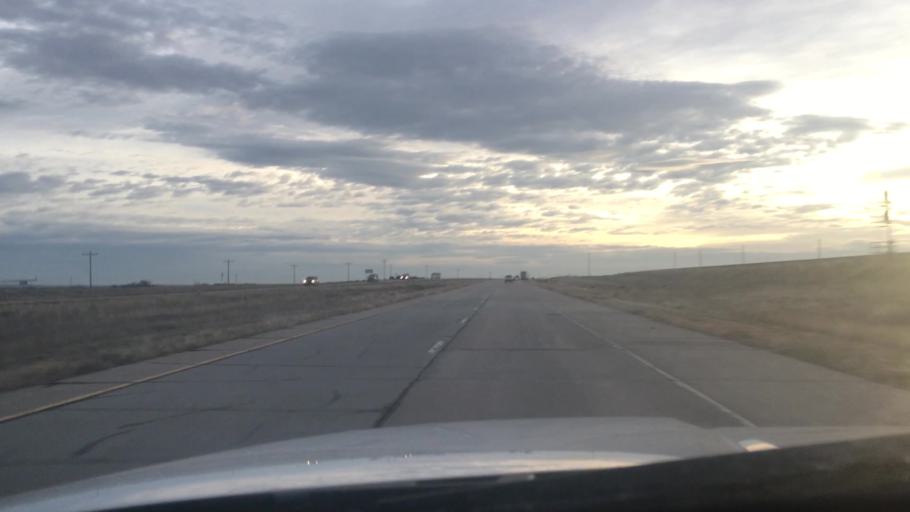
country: US
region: Colorado
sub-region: Morgan County
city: Fort Morgan
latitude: 40.2496
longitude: -104.0239
